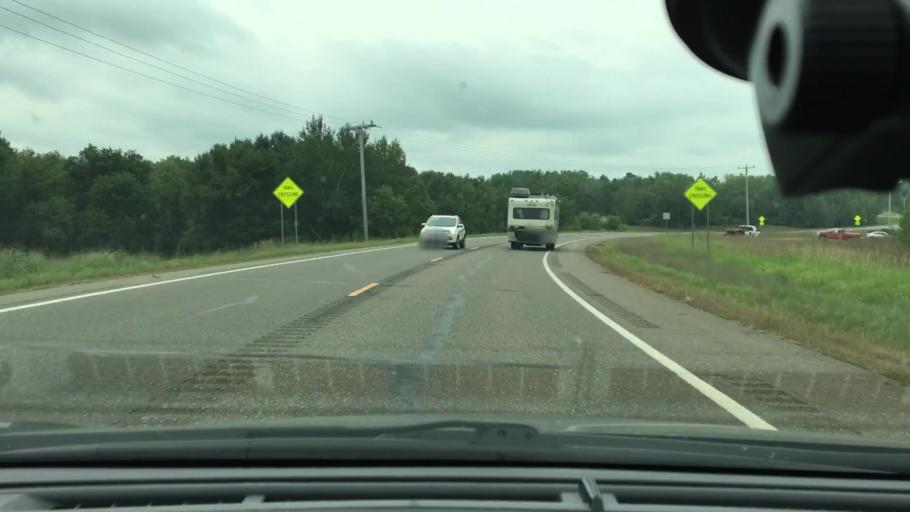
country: US
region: Minnesota
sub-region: Crow Wing County
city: Crosby
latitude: 46.4933
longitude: -93.9558
